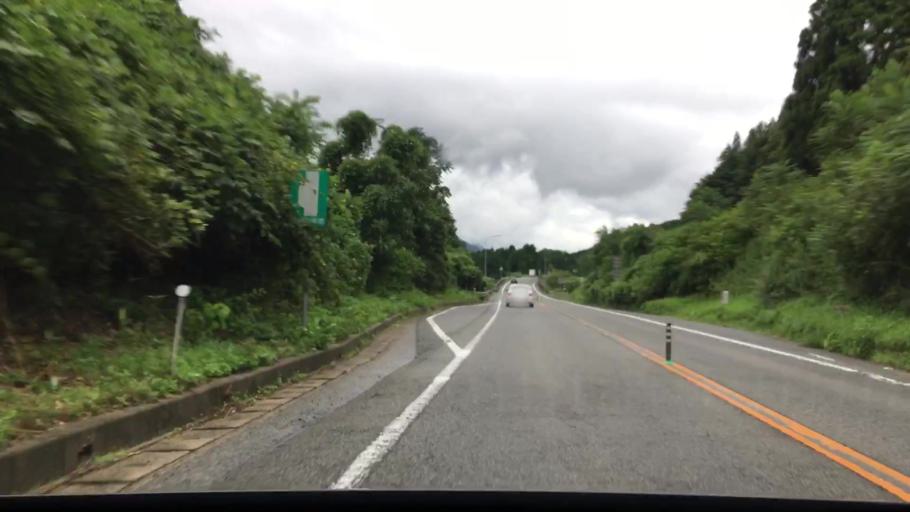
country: JP
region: Hyogo
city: Nishiwaki
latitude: 35.1013
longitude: 134.7773
